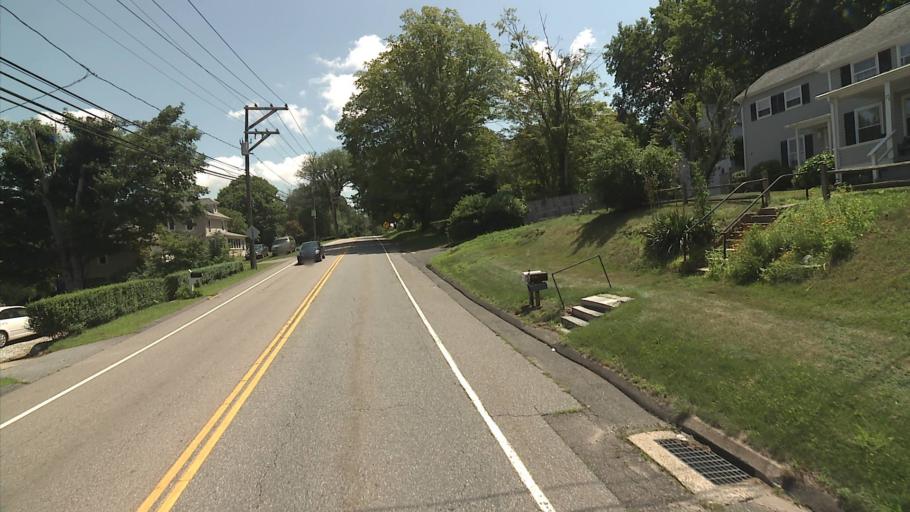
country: US
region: Connecticut
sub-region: Middlesex County
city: Chester Center
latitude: 41.3988
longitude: -72.4409
